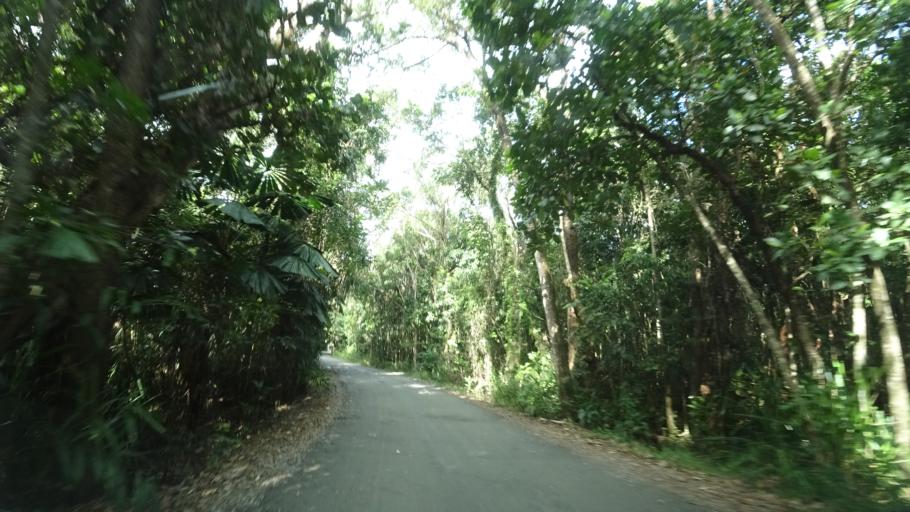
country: AU
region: Queensland
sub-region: Cairns
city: Port Douglas
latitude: -16.0960
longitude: 145.4620
